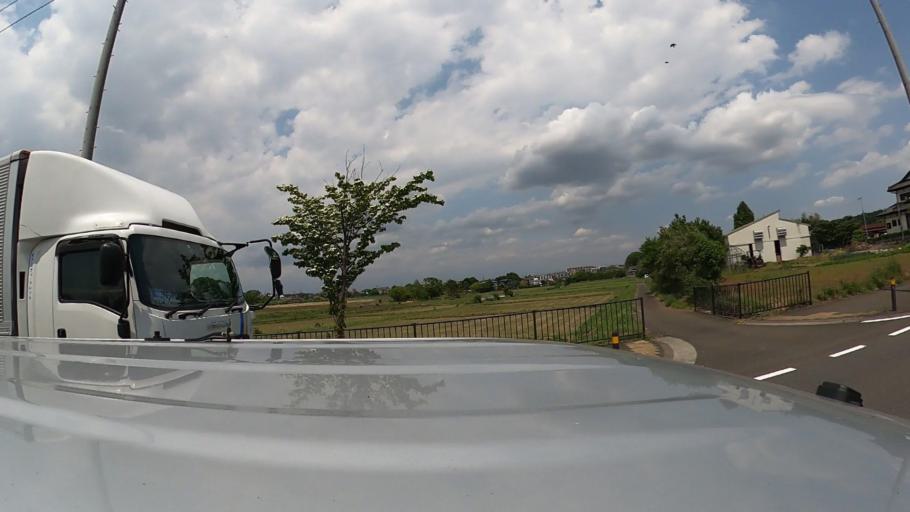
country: JP
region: Kanagawa
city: Chigasaki
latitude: 35.3936
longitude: 139.4133
